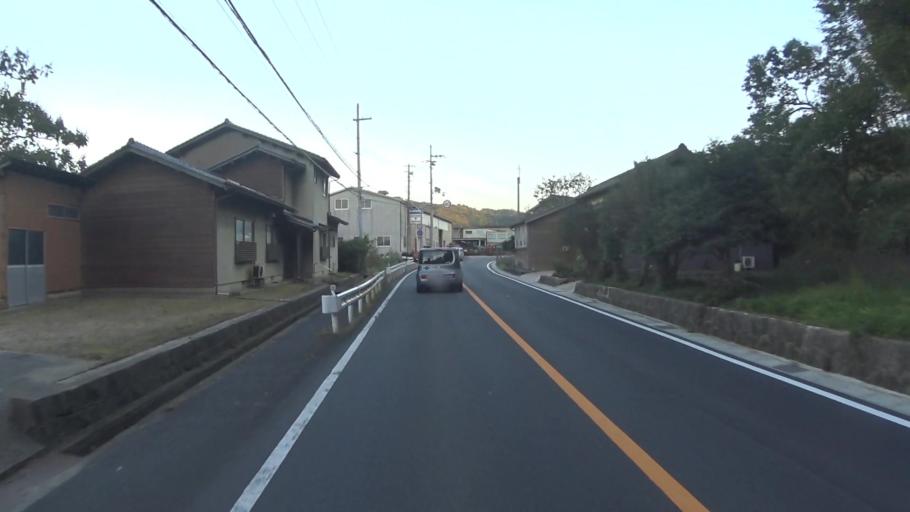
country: JP
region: Kyoto
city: Miyazu
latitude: 35.6639
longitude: 135.0292
